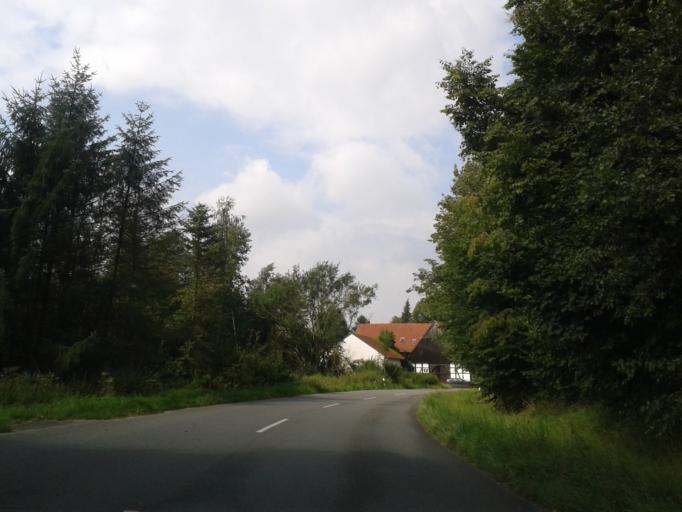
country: DE
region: North Rhine-Westphalia
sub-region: Regierungsbezirk Detmold
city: Blomberg
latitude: 51.9707
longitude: 9.0273
